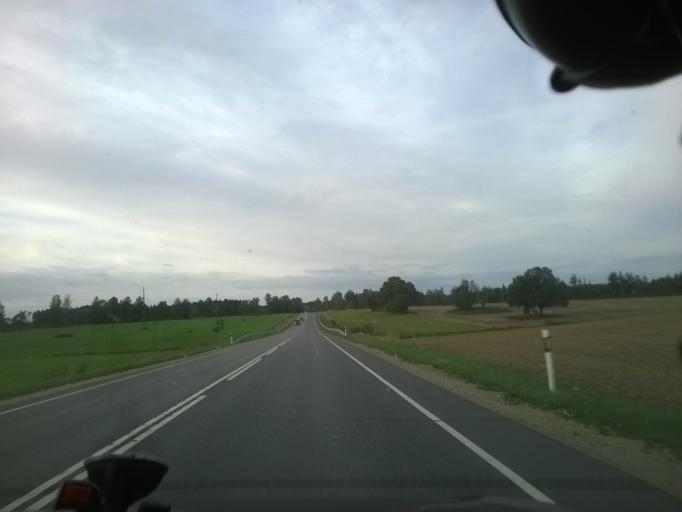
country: EE
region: Vorumaa
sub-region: Antsla vald
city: Vana-Antsla
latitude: 57.9908
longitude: 26.7660
